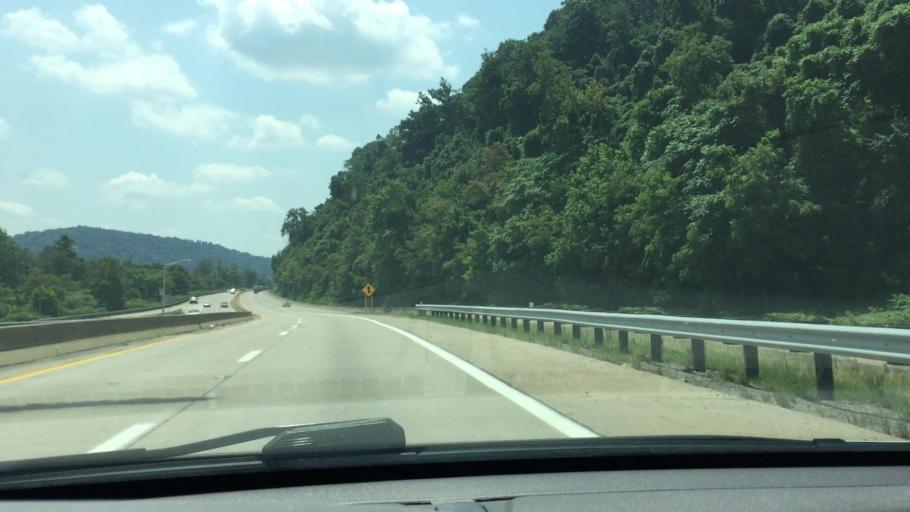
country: US
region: West Virginia
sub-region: Marshall County
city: McMechen
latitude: 39.9939
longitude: -80.7419
